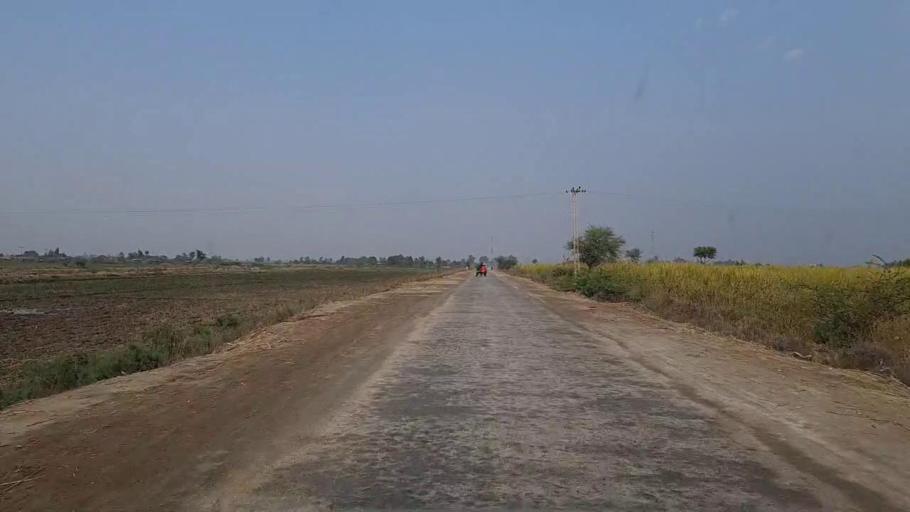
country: PK
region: Sindh
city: Mirwah Gorchani
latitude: 25.4199
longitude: 69.1483
